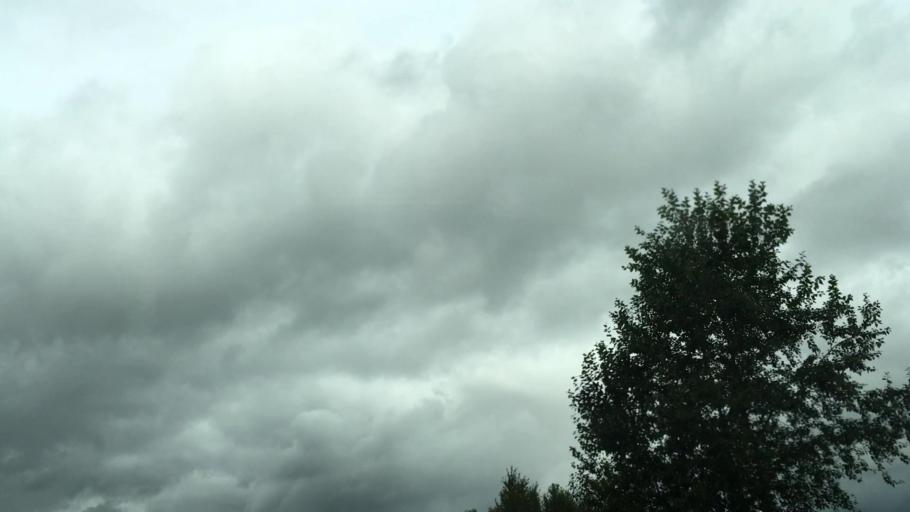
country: US
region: Washington
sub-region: Snohomish County
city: Fobes Hill
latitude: 47.9224
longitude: -122.1527
